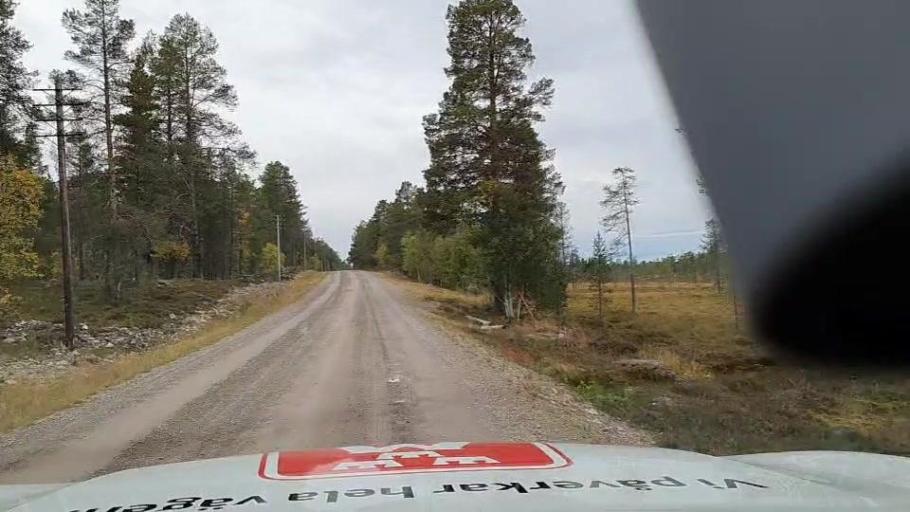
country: NO
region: Hedmark
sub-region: Engerdal
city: Engerdal
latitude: 62.0544
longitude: 12.7325
